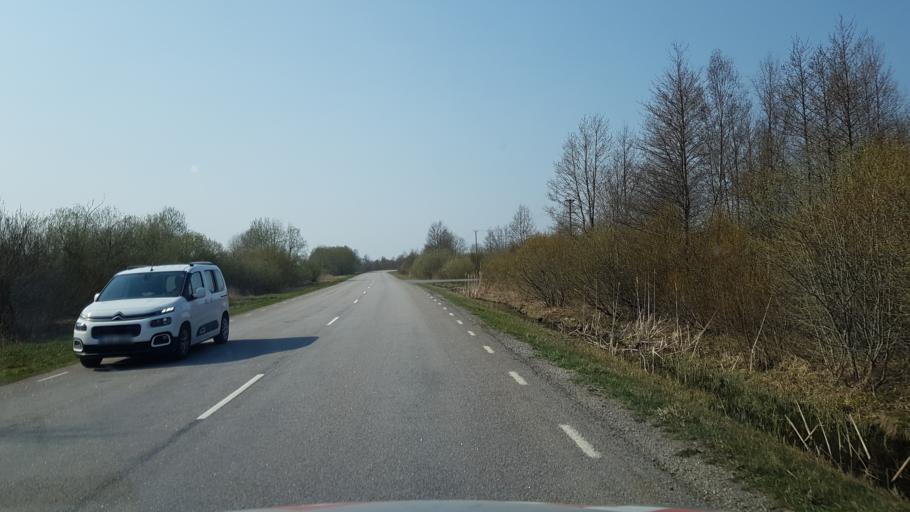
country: EE
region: Harju
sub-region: Paldiski linn
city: Paldiski
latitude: 59.3221
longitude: 24.1268
